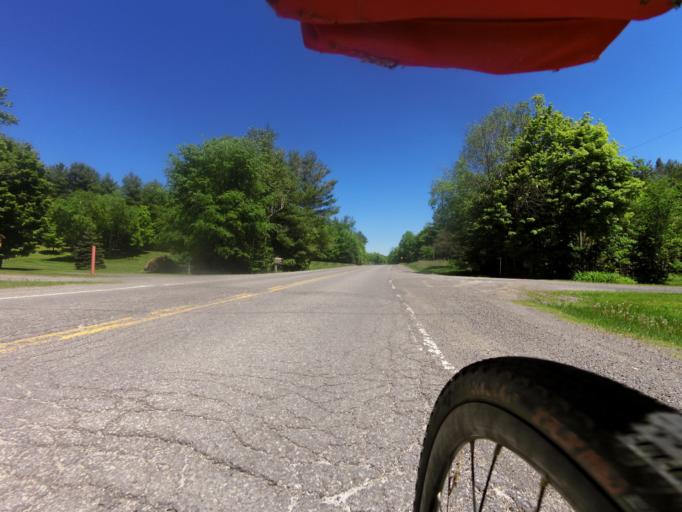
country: CA
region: Ontario
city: Carleton Place
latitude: 45.1848
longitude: -76.3590
